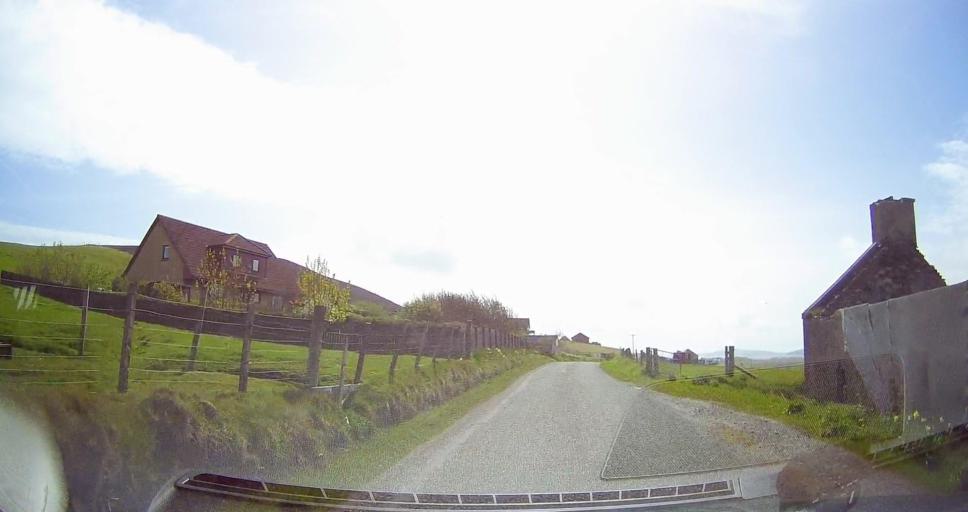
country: GB
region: Scotland
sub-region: Shetland Islands
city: Sandwick
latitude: 60.0536
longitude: -1.2236
